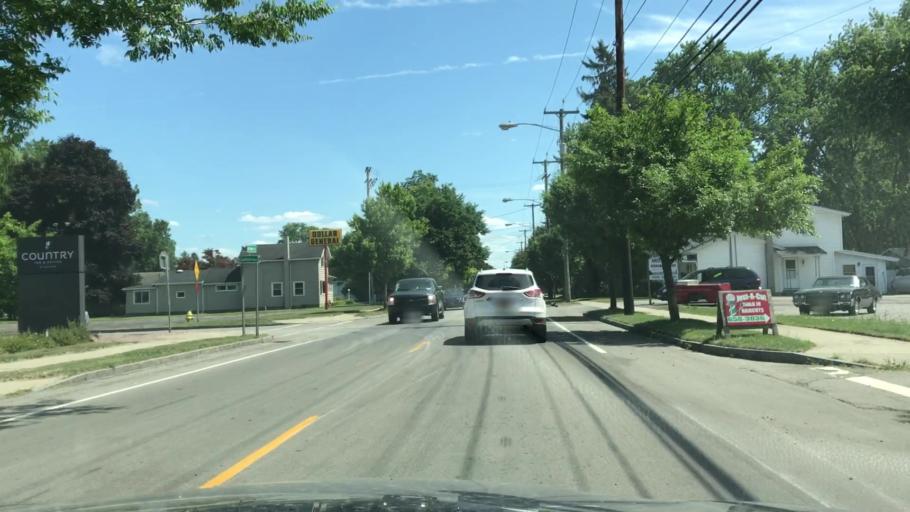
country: US
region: New York
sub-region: Livingston County
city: Mount Morris
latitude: 42.7365
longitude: -77.8806
